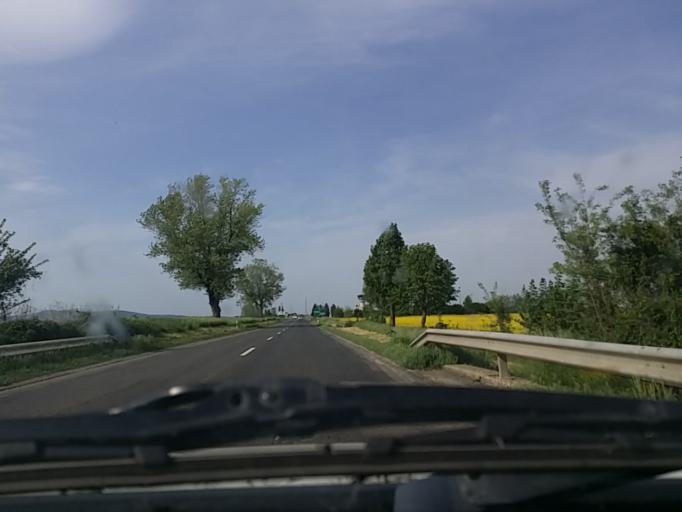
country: HU
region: Baranya
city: Kozarmisleny
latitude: 45.9887
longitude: 18.2309
